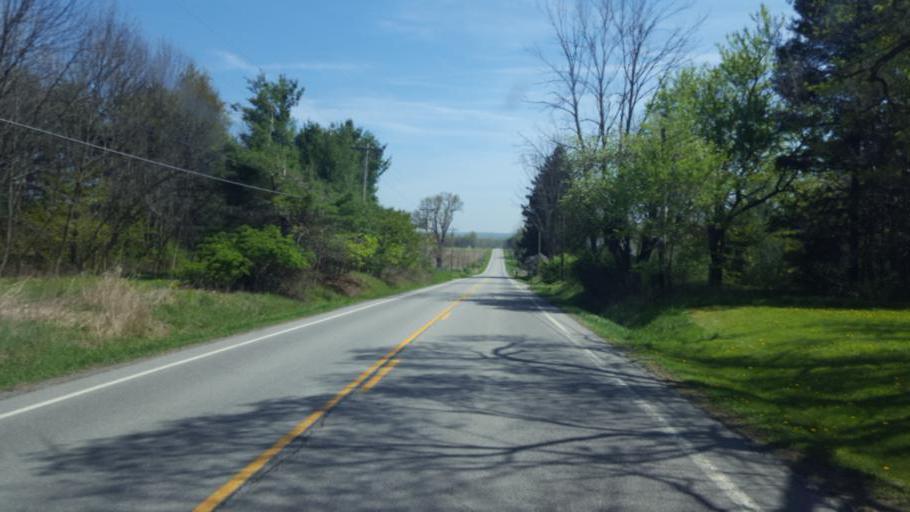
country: US
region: Ohio
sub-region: Wayne County
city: West Salem
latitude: 41.0033
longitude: -82.0646
